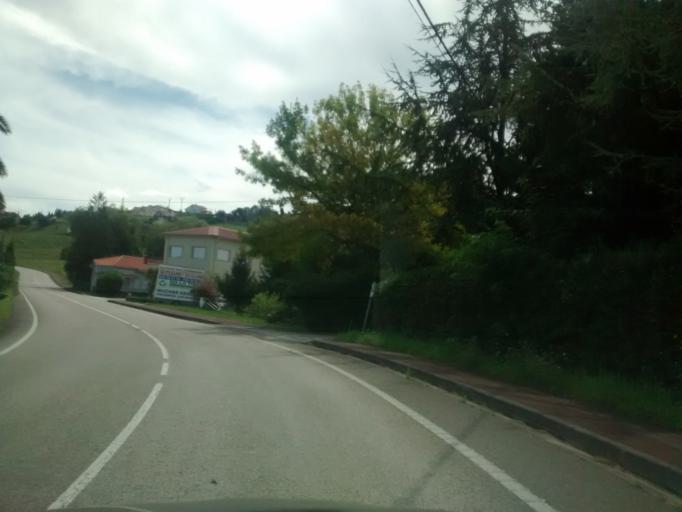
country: ES
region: Cantabria
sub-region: Provincia de Cantabria
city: Miengo
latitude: 43.4117
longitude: -3.9591
